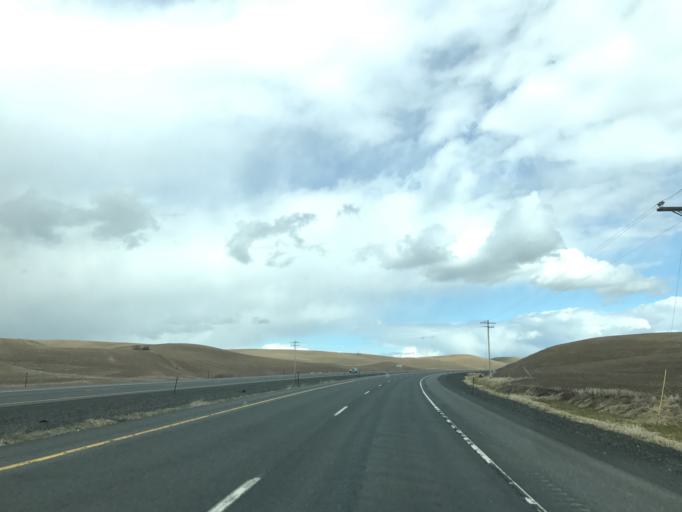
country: US
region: Idaho
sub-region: Nez Perce County
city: Lewiston
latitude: 46.5047
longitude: -116.9928
